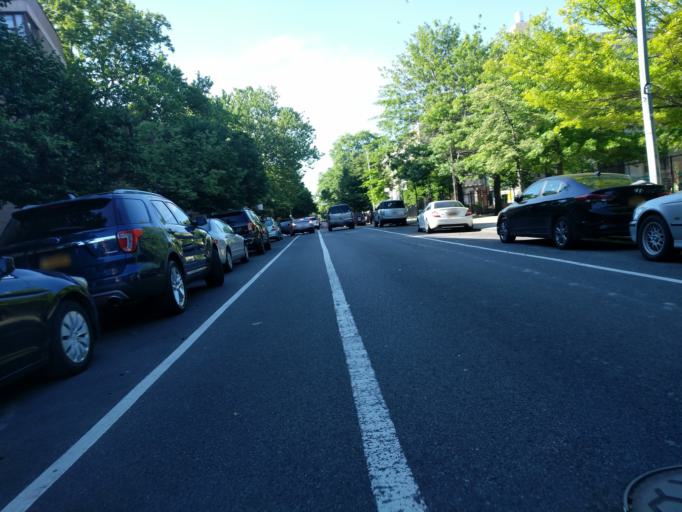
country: US
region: New York
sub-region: Queens County
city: Long Island City
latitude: 40.7091
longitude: -73.9452
